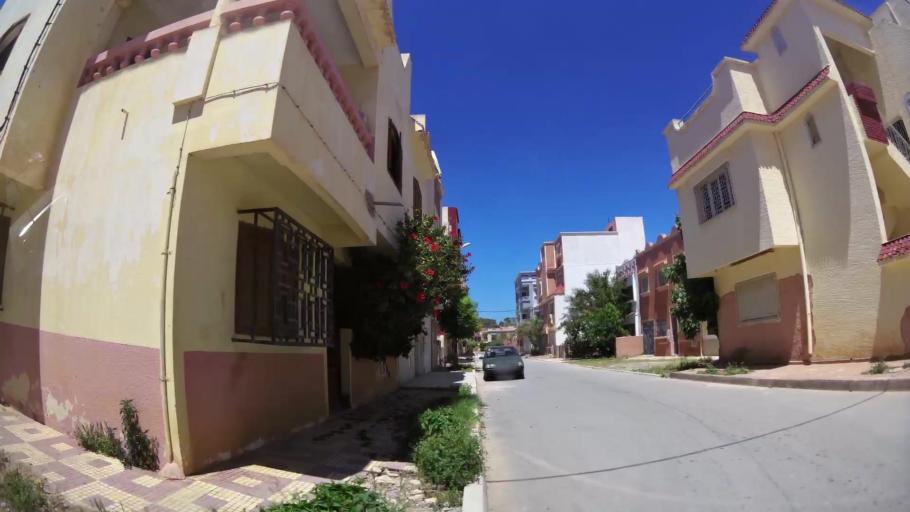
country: MA
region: Oriental
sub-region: Berkane-Taourirt
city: Madagh
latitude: 35.0805
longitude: -2.2213
